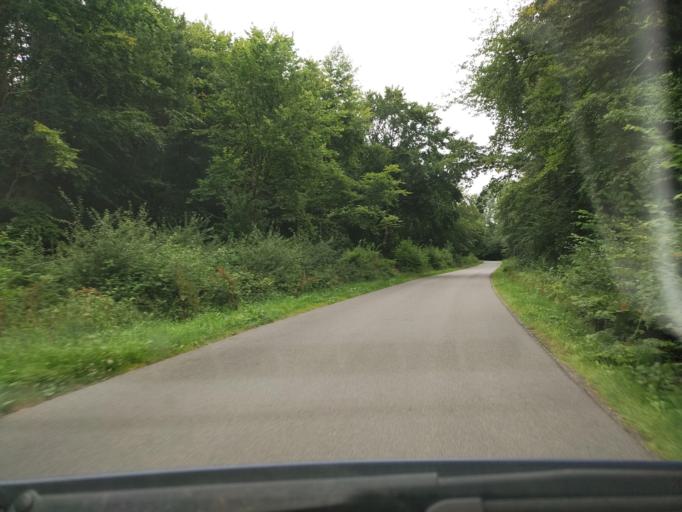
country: DE
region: Schleswig-Holstein
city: Neuberend
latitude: 54.5207
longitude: 9.5257
